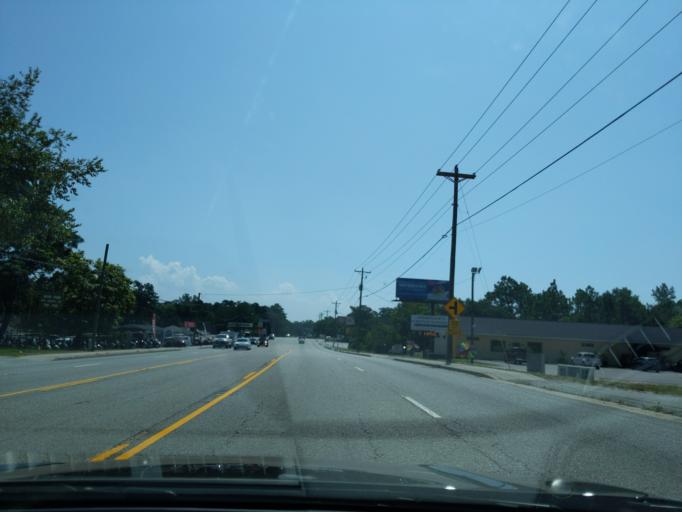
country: US
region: South Carolina
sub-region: Lexington County
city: Oak Grove
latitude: 33.9719
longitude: -81.1457
